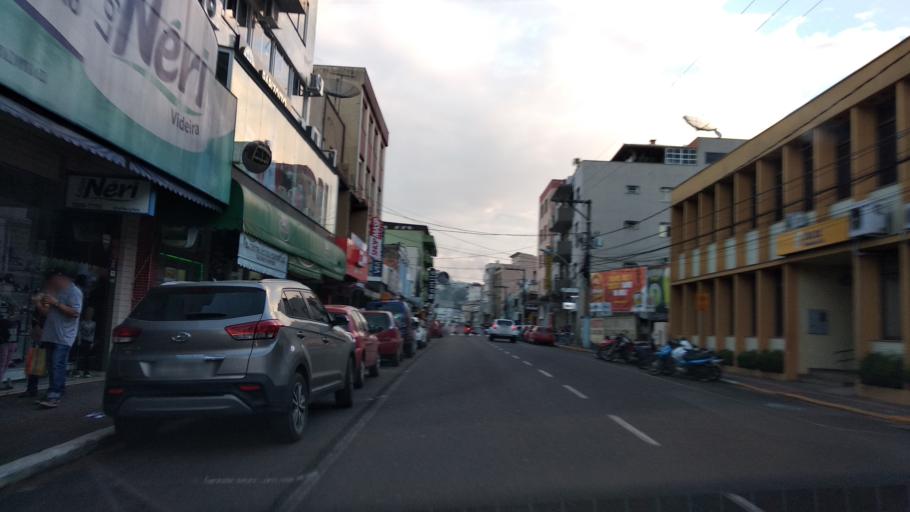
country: BR
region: Santa Catarina
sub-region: Videira
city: Videira
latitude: -27.0035
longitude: -51.1570
